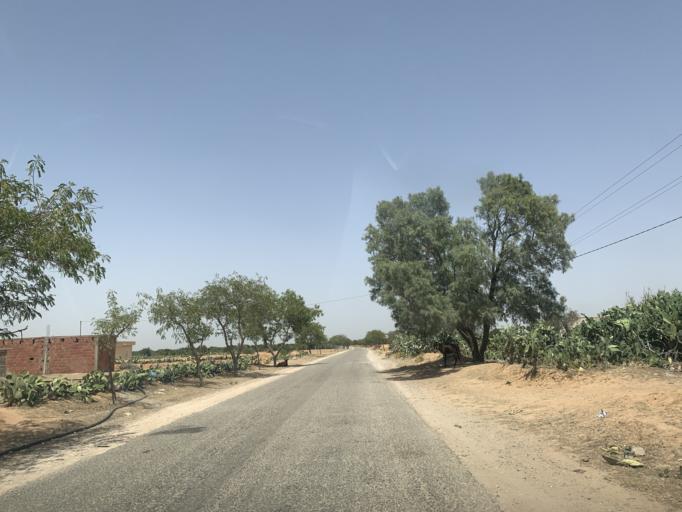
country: TN
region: Al Mahdiyah
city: Shurban
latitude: 35.1888
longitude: 10.2454
